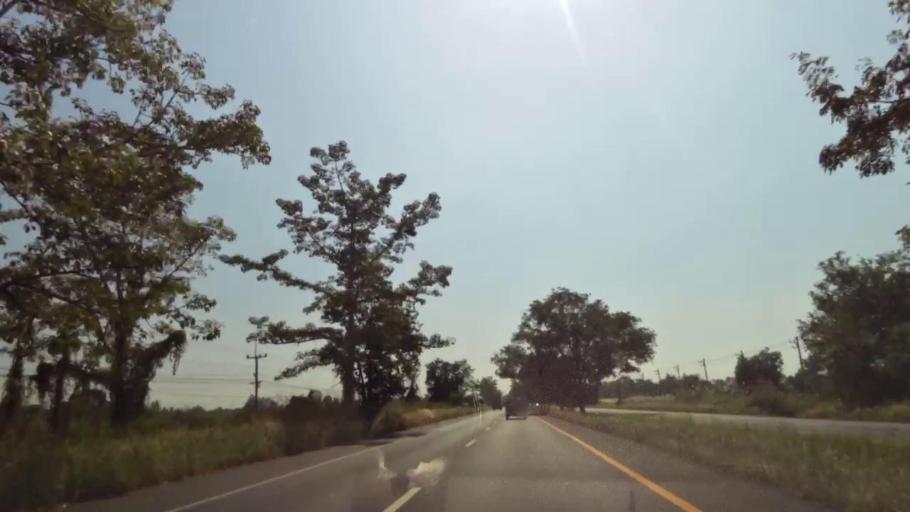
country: TH
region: Nakhon Sawan
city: Kao Liao
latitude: 15.9453
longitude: 100.1146
